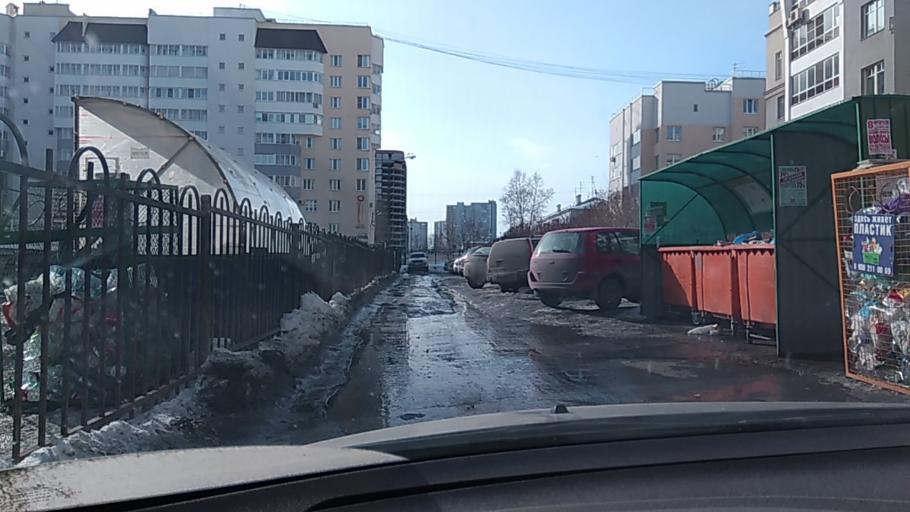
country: RU
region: Sverdlovsk
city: Yekaterinburg
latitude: 56.8083
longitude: 60.6194
